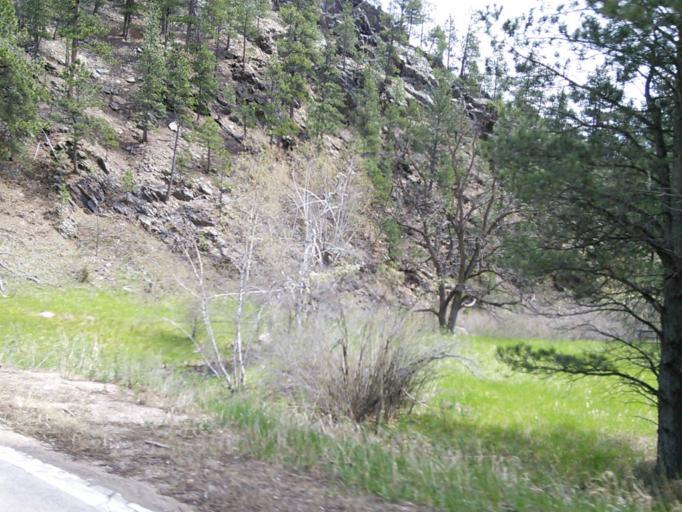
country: US
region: South Dakota
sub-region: Pennington County
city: Colonial Pine Hills
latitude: 43.8738
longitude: -103.3789
